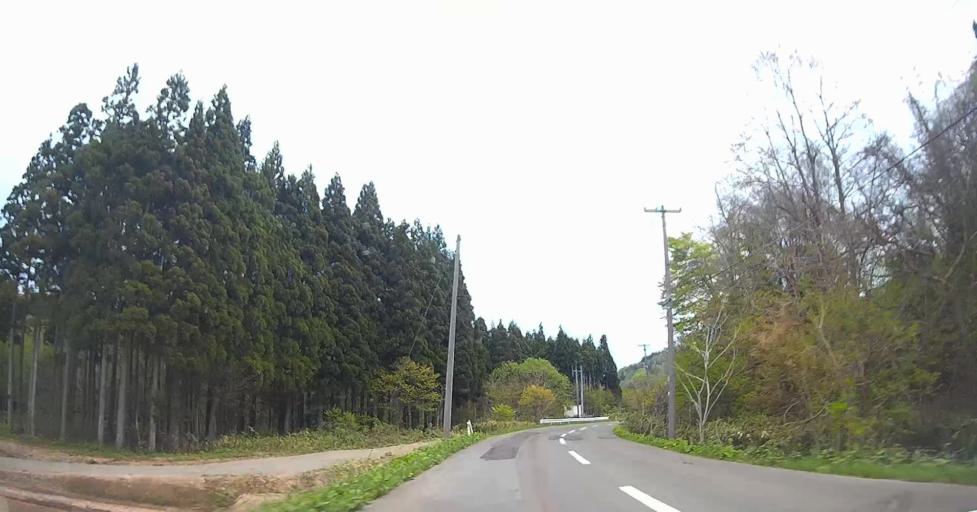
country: JP
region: Aomori
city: Goshogawara
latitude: 41.1212
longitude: 140.5231
